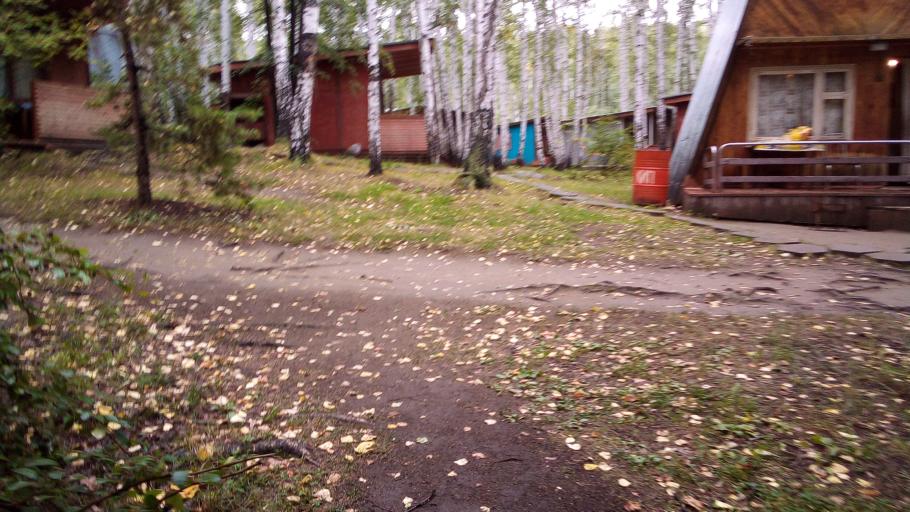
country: RU
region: Chelyabinsk
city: Tayginka
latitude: 55.4766
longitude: 60.4968
